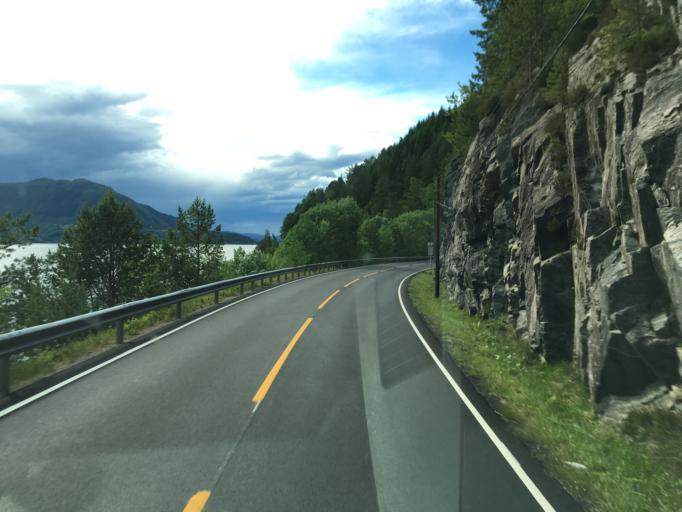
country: NO
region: More og Romsdal
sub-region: Tingvoll
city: Tingvoll
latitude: 62.9561
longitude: 8.1144
